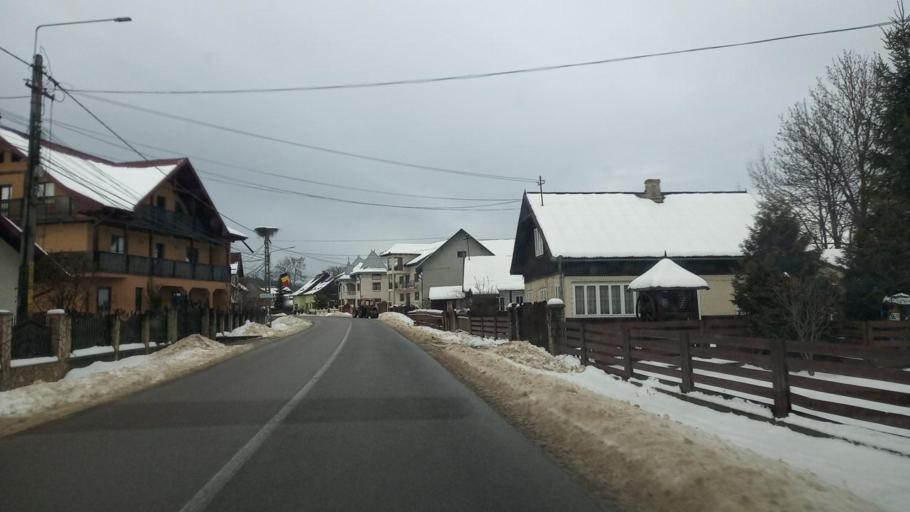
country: RO
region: Suceava
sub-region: Comuna Manastirea Humorului
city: Manastirea Humorului
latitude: 47.5907
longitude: 25.8659
